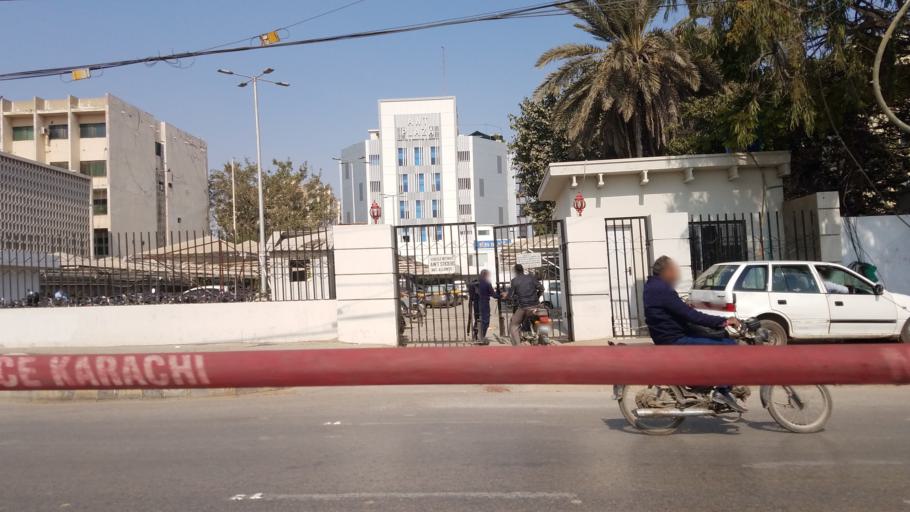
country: PK
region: Sindh
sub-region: Karachi District
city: Karachi
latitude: 24.8504
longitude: 67.0134
